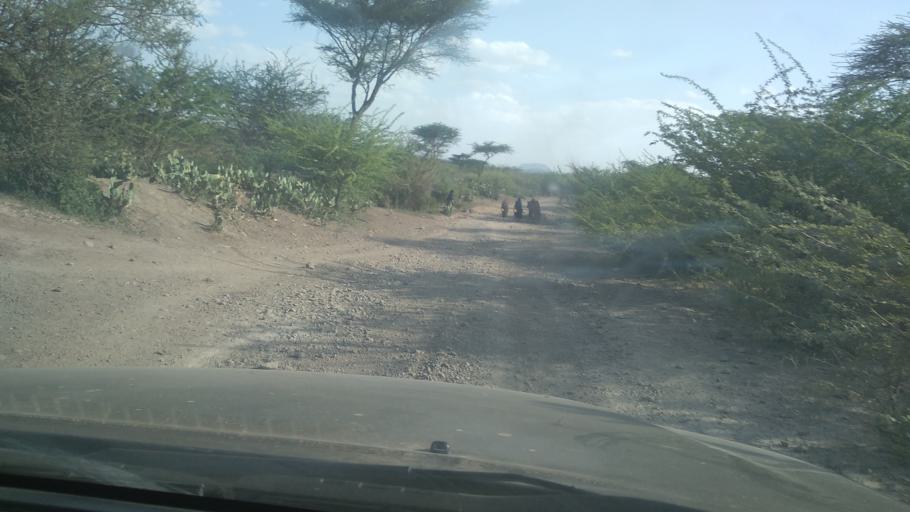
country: ET
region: Oromiya
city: Hirna
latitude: 9.4598
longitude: 40.9955
